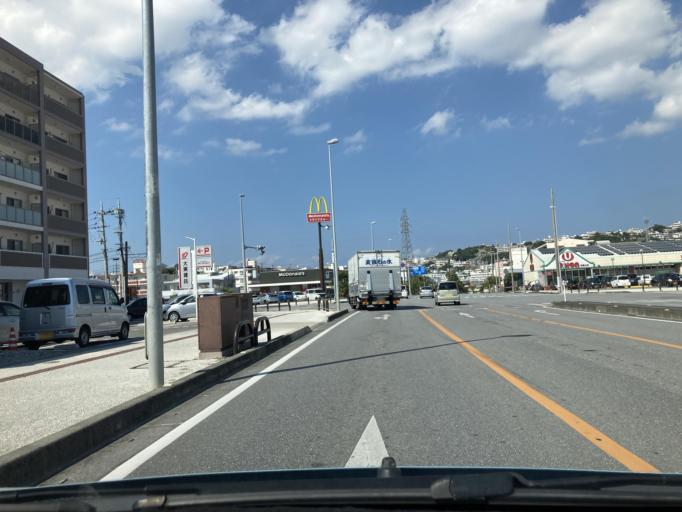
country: JP
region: Okinawa
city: Tomigusuku
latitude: 26.1916
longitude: 127.7144
